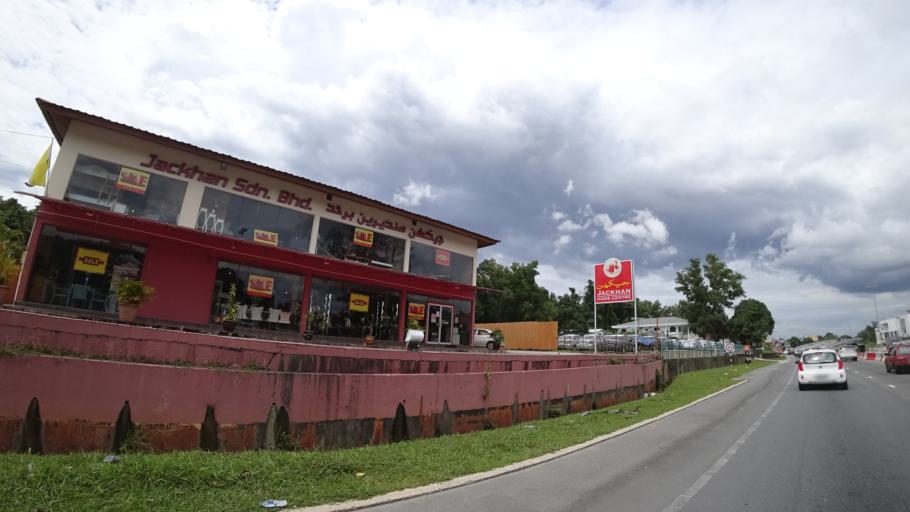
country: BN
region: Brunei and Muara
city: Bandar Seri Begawan
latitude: 4.8809
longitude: 114.8886
